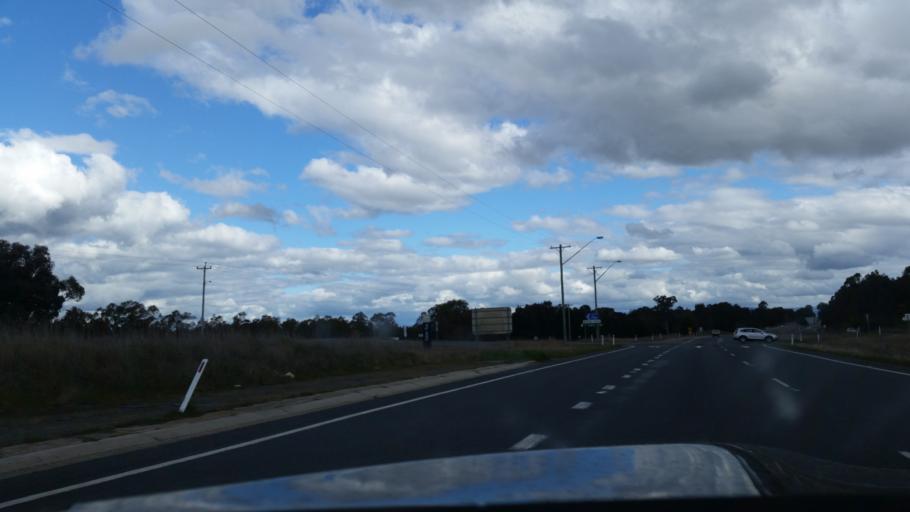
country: AU
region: New South Wales
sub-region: Albury Municipality
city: Lavington
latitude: -35.9713
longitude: 147.0044
